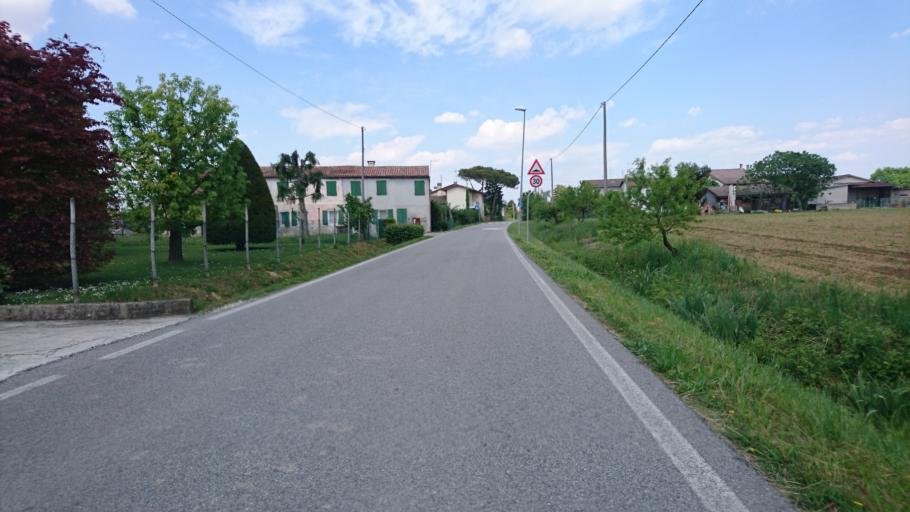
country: IT
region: Veneto
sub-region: Provincia di Padova
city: Saccolongo
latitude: 45.4032
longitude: 11.7310
